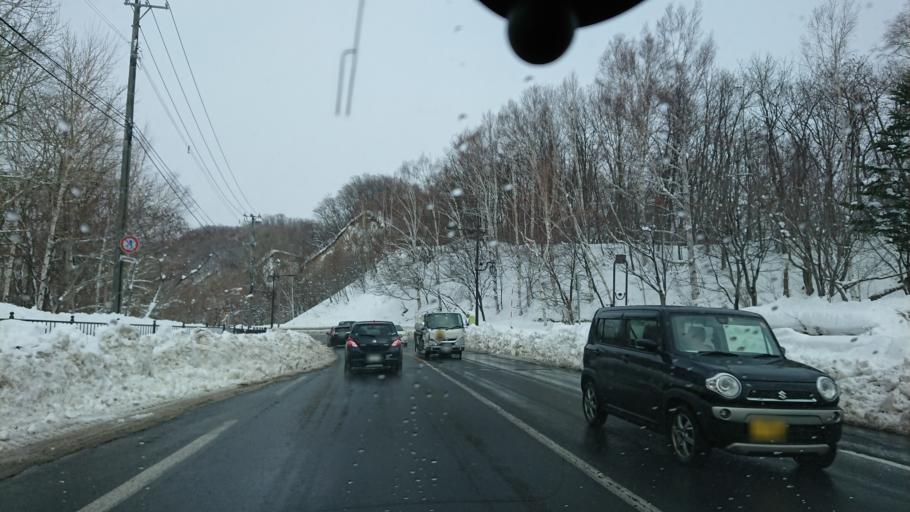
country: JP
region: Hokkaido
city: Sapporo
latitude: 42.9762
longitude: 141.3445
